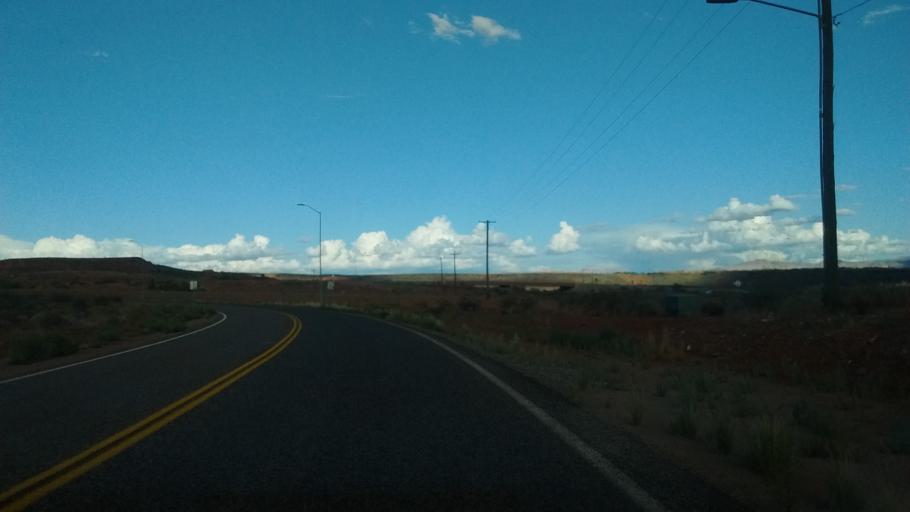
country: US
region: Utah
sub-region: Washington County
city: Washington
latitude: 37.1459
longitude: -113.4939
